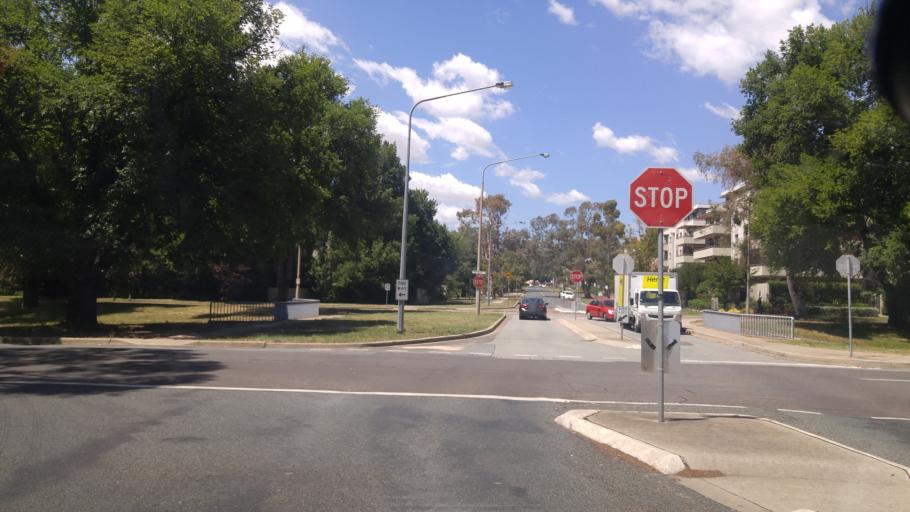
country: AU
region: Australian Capital Territory
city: Forrest
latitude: -35.3090
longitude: 149.1352
